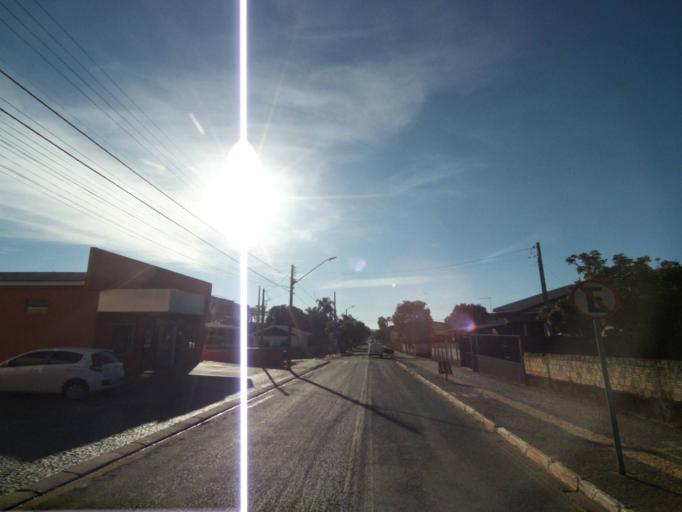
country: BR
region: Parana
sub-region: Tibagi
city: Tibagi
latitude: -24.5203
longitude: -50.4070
